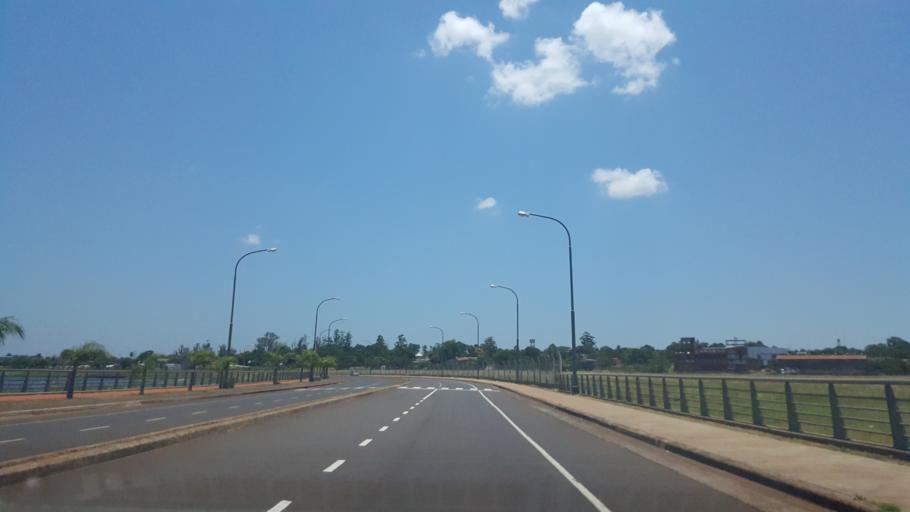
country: AR
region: Misiones
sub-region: Departamento de Capital
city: Posadas
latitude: -27.4101
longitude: -55.8964
